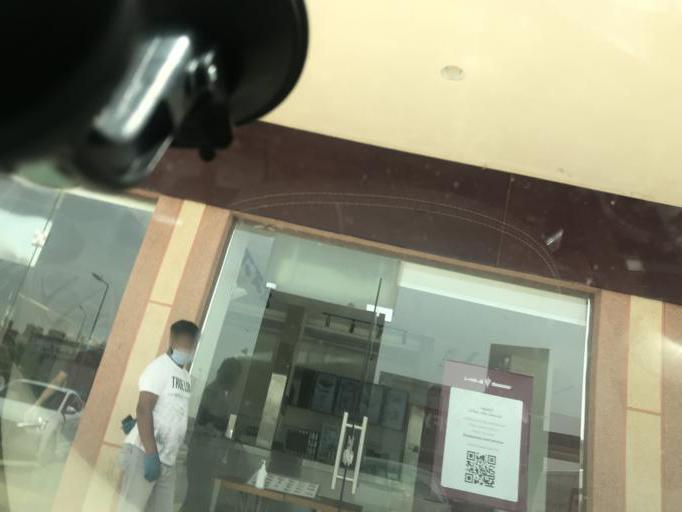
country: SA
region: Ar Riyad
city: Riyadh
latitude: 24.8033
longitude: 46.6049
